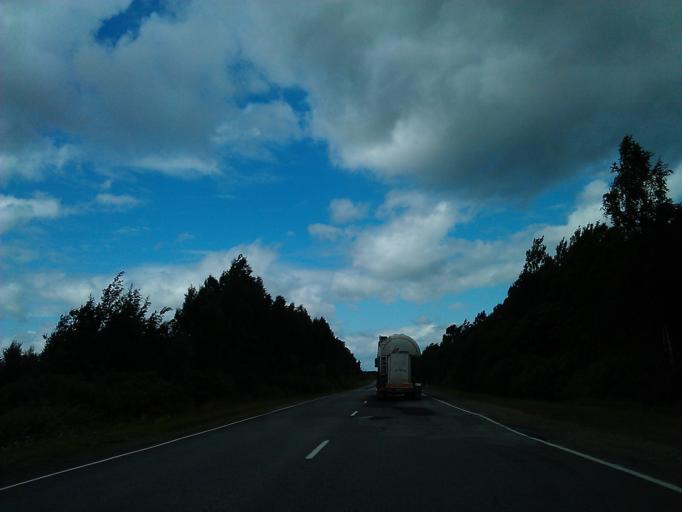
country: LV
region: Tukuma Rajons
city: Tukums
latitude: 56.9354
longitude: 23.1896
